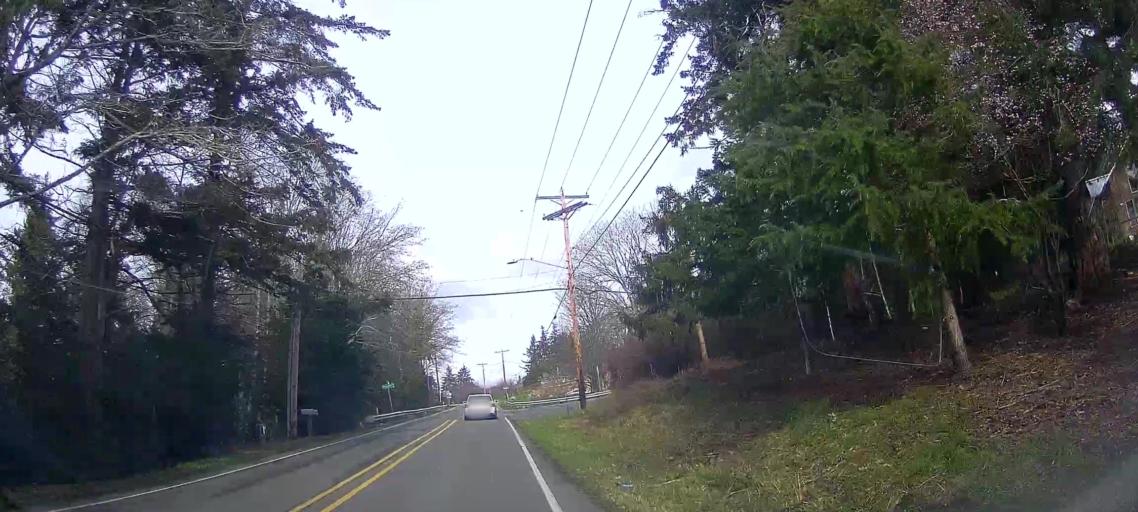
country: US
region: Washington
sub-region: Island County
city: Camano
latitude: 48.1752
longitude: -122.5282
